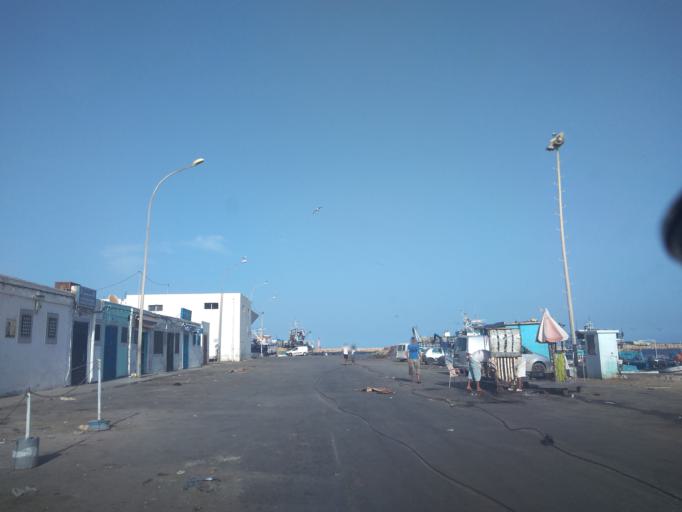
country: TN
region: Safaqis
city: Sfax
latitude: 34.7132
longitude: 10.7640
